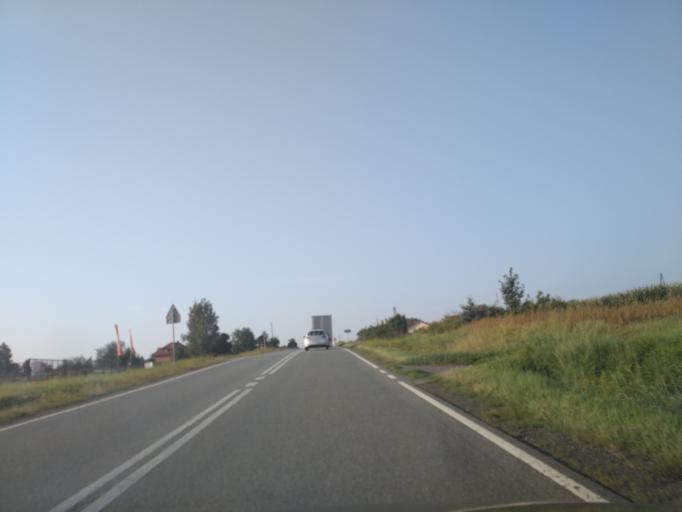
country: PL
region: Lublin Voivodeship
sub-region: Powiat janowski
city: Modliborzyce
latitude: 50.7975
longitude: 22.3184
